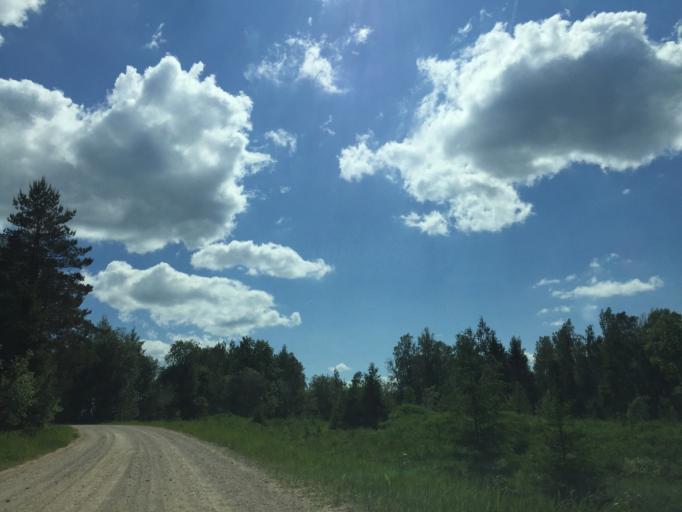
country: LV
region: Priekuli
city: Priekuli
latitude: 57.2459
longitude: 25.4378
